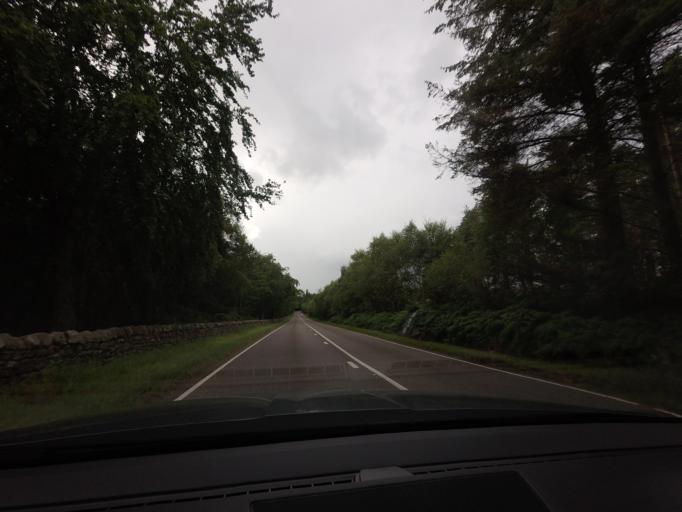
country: GB
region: Scotland
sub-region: Moray
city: Findochty
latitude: 57.6799
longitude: -2.8931
